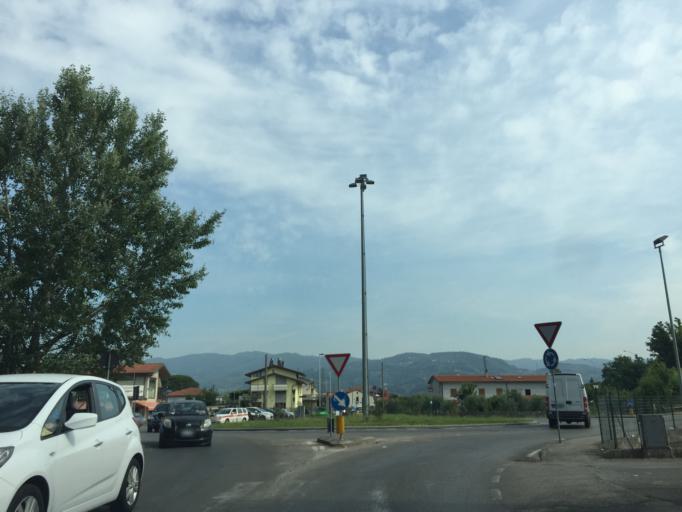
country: IT
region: Tuscany
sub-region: Provincia di Pistoia
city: Montecatini-Terme
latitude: 43.8681
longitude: 10.7671
